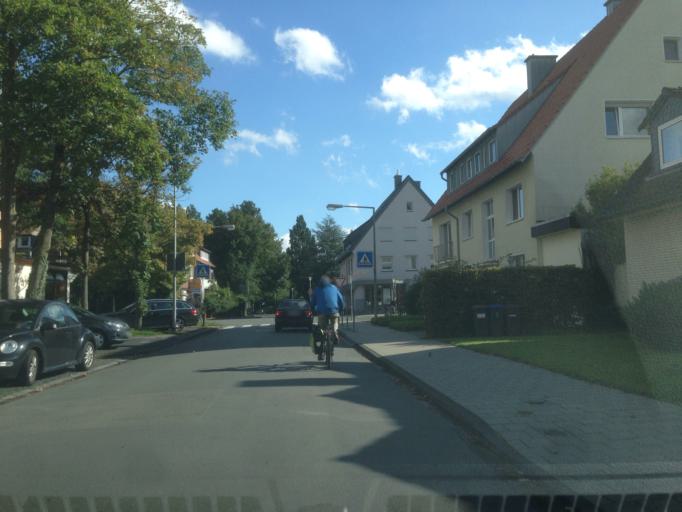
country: DE
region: North Rhine-Westphalia
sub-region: Regierungsbezirk Munster
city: Muenster
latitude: 51.9565
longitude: 7.5923
